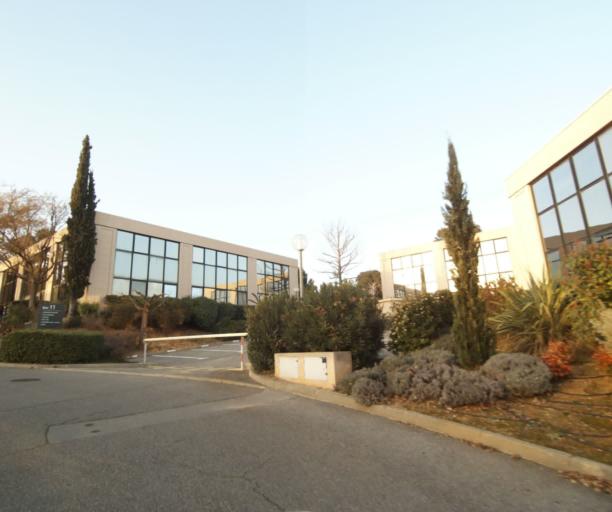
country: FR
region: Provence-Alpes-Cote d'Azur
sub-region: Departement des Bouches-du-Rhone
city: Vitrolles
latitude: 43.4307
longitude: 5.2723
